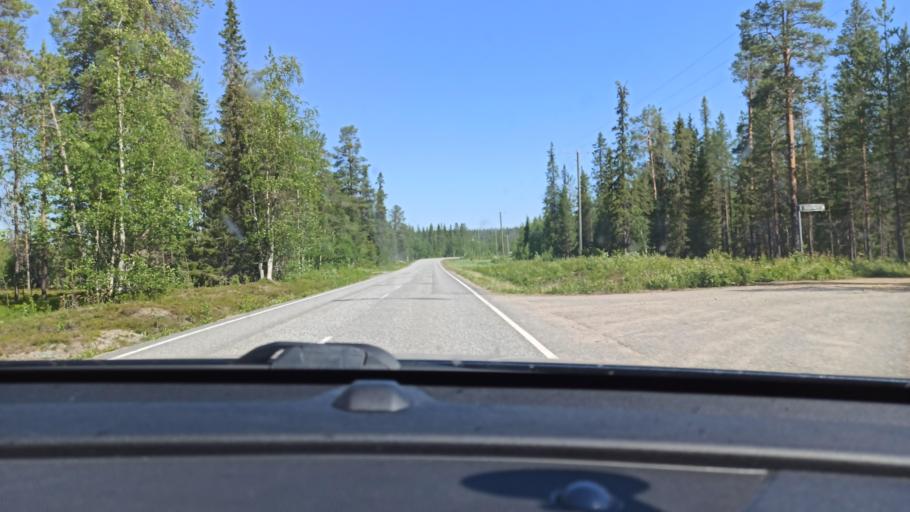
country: FI
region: Lapland
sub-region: Tunturi-Lappi
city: Kolari
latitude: 67.6281
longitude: 24.1559
